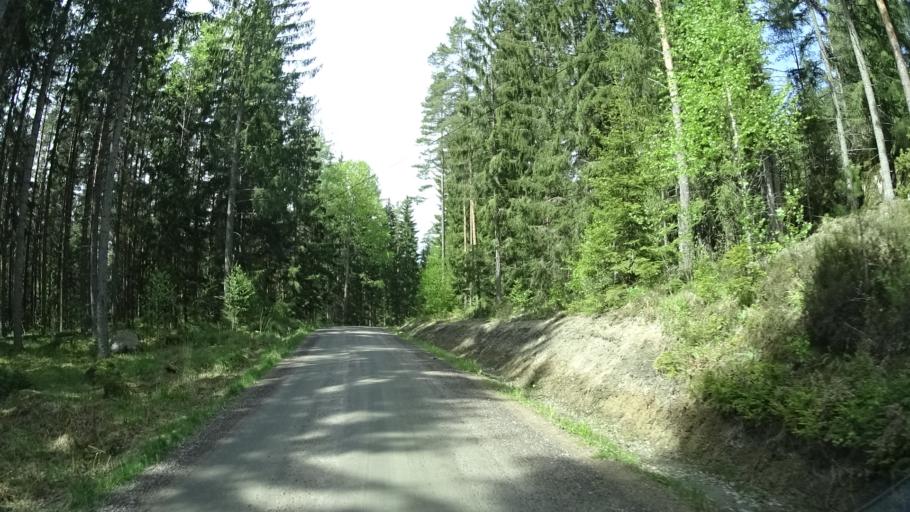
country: SE
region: OEstergoetland
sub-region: Finspangs Kommun
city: Finspang
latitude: 58.7658
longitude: 15.8413
